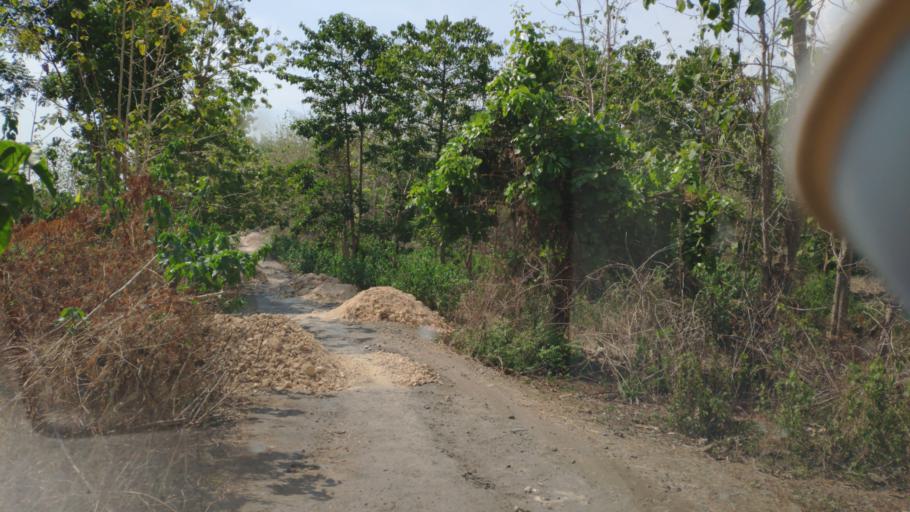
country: ID
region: Central Java
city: Balong Wetan
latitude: -6.9976
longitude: 111.2709
